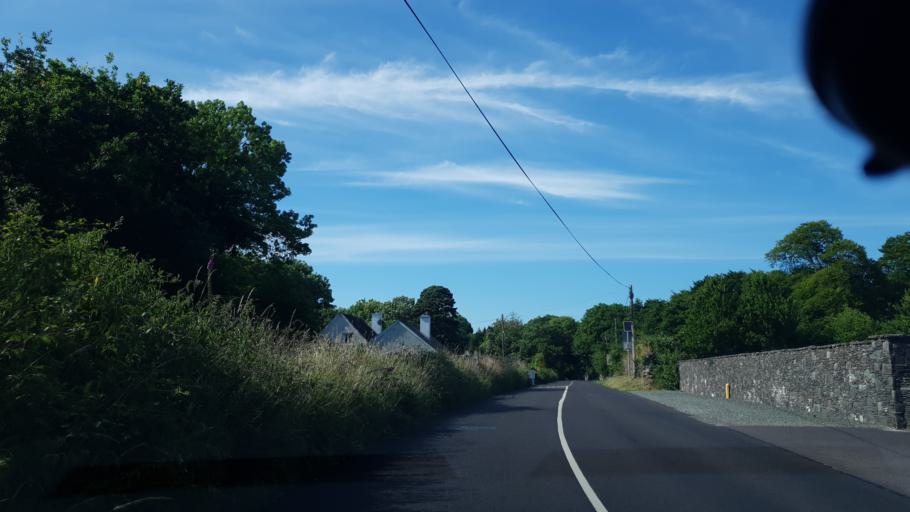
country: IE
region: Munster
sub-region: Ciarrai
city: Cill Airne
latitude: 52.0739
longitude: -9.5082
